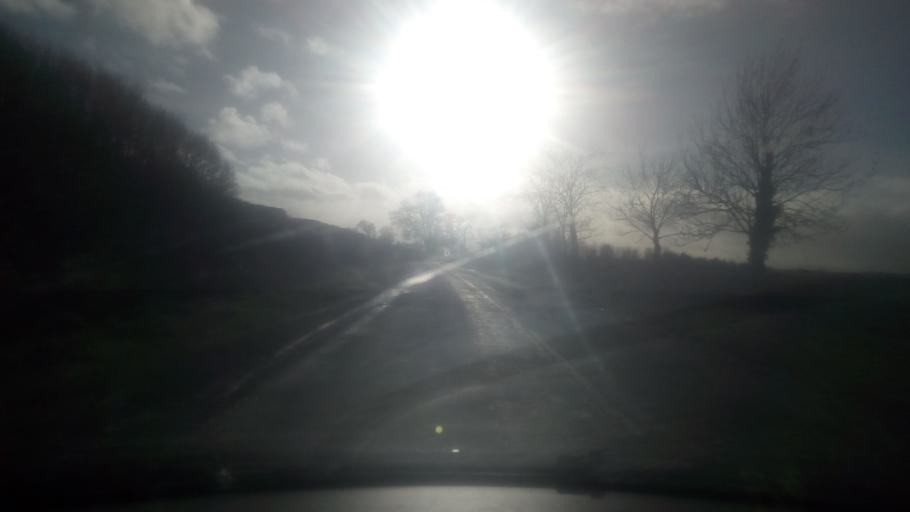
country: GB
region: Scotland
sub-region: The Scottish Borders
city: Coldstream
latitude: 55.7074
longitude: -2.2912
